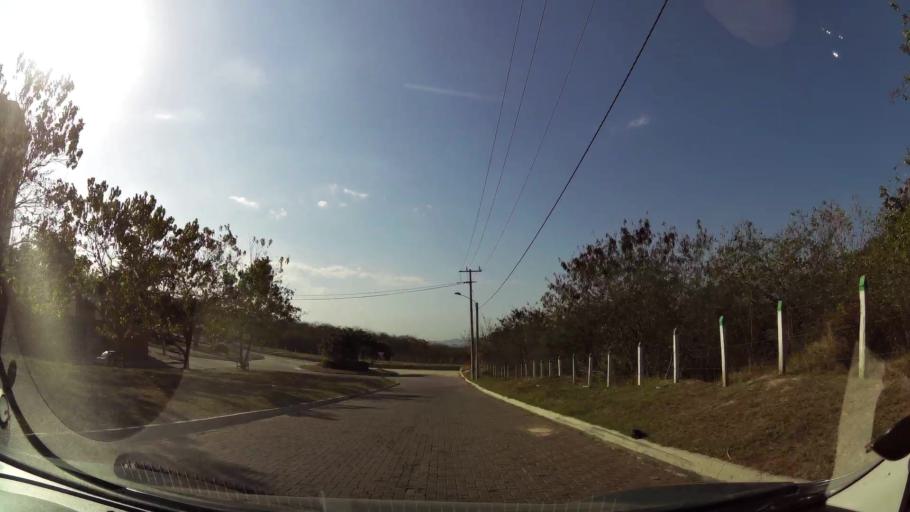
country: CO
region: Atlantico
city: Barranquilla
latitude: 10.9994
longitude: -74.8372
